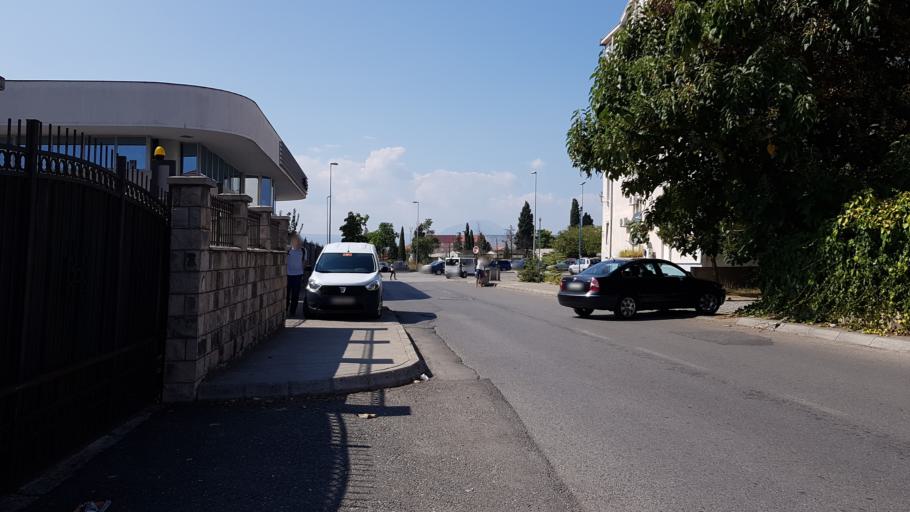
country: ME
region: Podgorica
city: Podgorica
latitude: 42.4337
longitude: 19.2752
